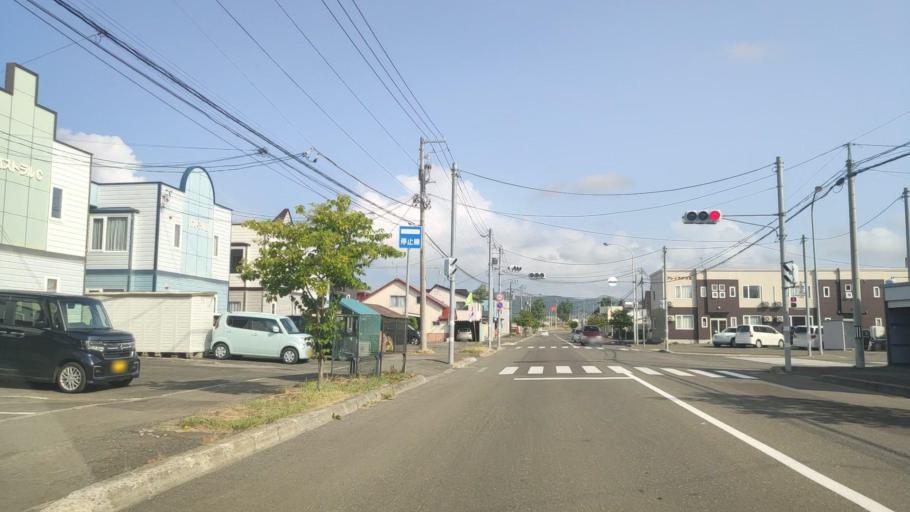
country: JP
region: Hokkaido
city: Shimo-furano
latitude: 43.3515
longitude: 142.3913
